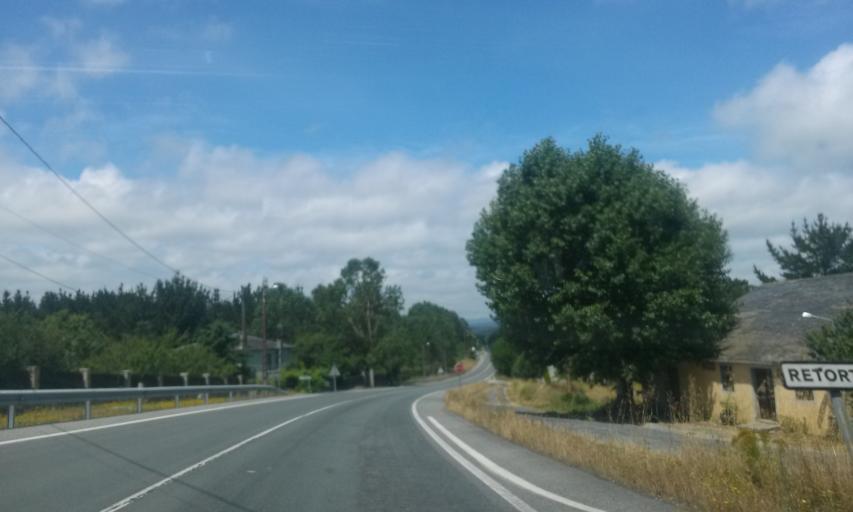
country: ES
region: Galicia
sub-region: Provincia de Lugo
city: Friol
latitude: 43.0281
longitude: -7.6969
